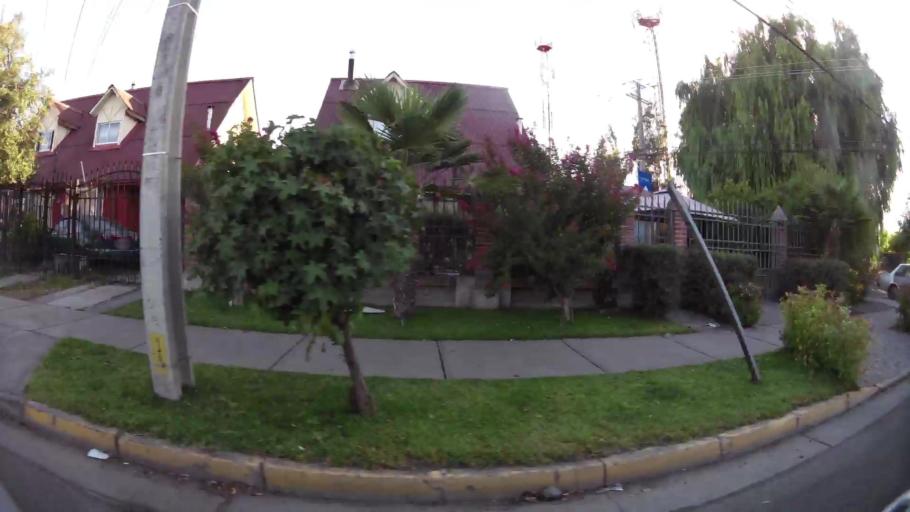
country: CL
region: Maule
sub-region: Provincia de Talca
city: Talca
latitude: -35.4490
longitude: -71.6779
